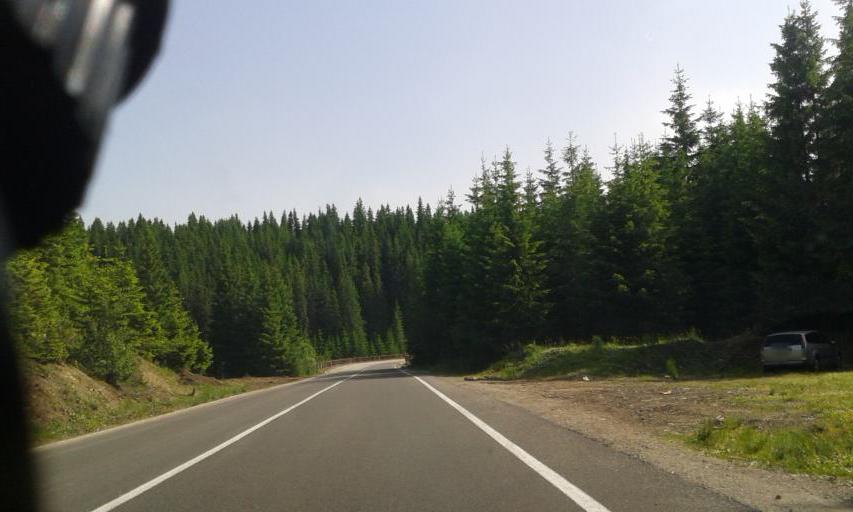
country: RO
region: Alba
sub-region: Comuna Sugag
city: Sugag
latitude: 45.5633
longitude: 23.6218
